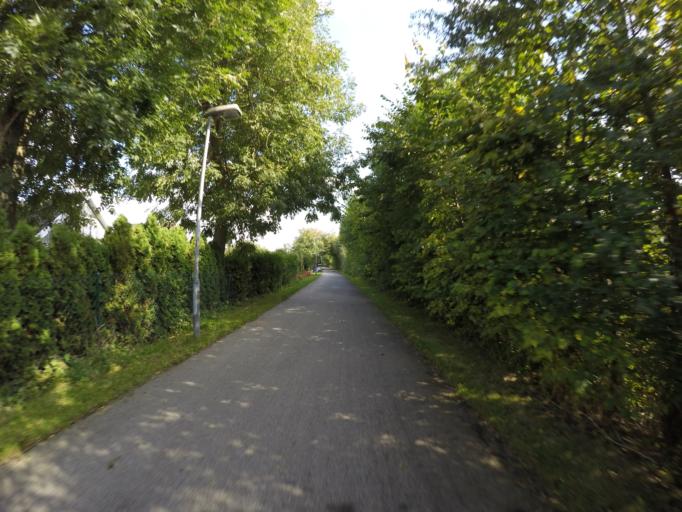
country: SE
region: Skane
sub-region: Burlovs Kommun
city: Arloev
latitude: 55.5861
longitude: 13.0872
